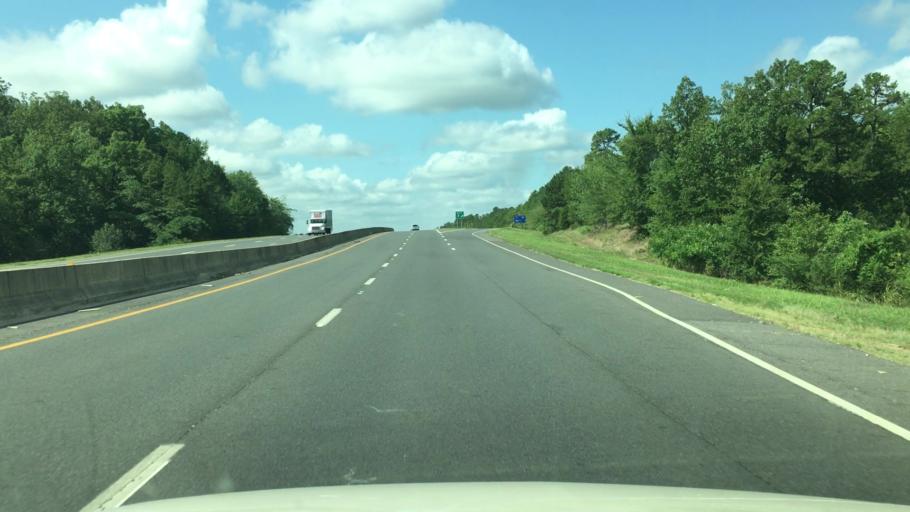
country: US
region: Arkansas
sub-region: Garland County
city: Piney
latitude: 34.4828
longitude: -93.1135
